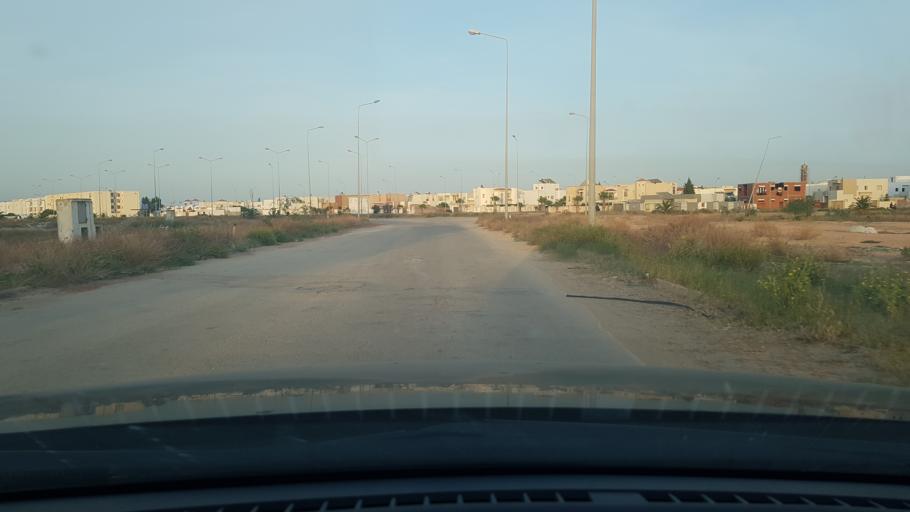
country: TN
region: Safaqis
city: Al Qarmadah
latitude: 34.8307
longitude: 10.7526
